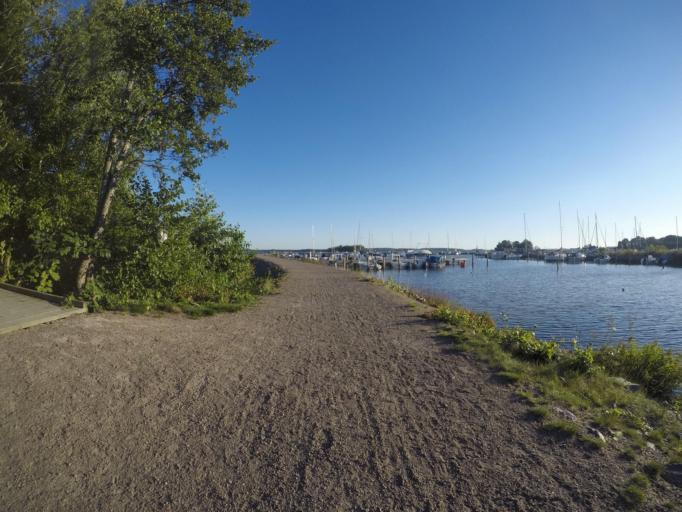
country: SE
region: Vaestmanland
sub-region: Vasteras
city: Vasteras
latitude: 59.5484
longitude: 16.6585
